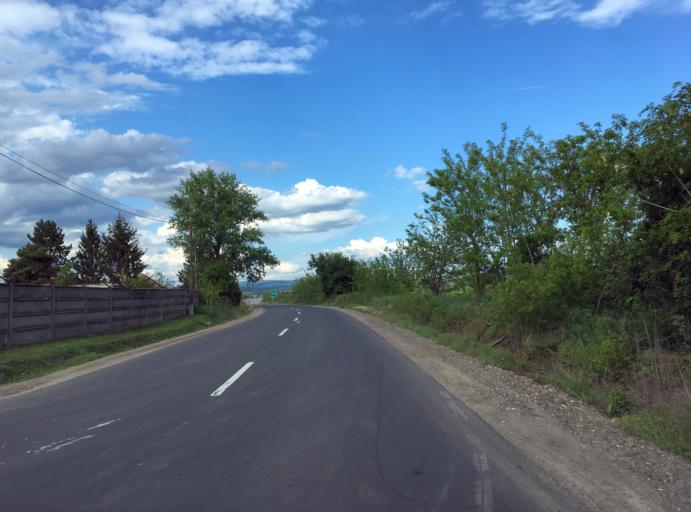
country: HU
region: Heves
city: Lorinci
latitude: 47.7267
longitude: 19.6592
